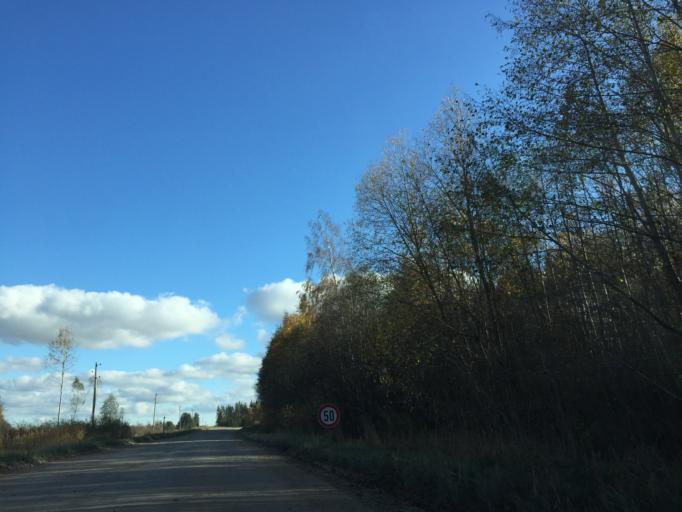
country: LV
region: Tukuma Rajons
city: Tukums
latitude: 56.9616
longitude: 23.0020
